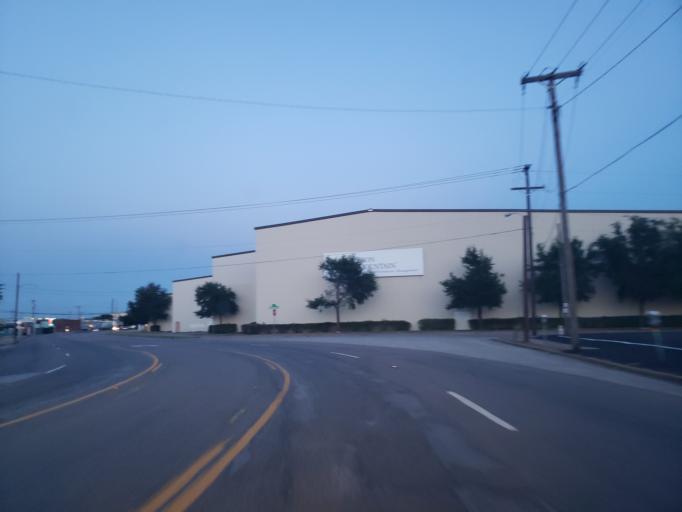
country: US
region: Texas
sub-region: Dallas County
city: Dallas
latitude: 32.7657
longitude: -96.7928
